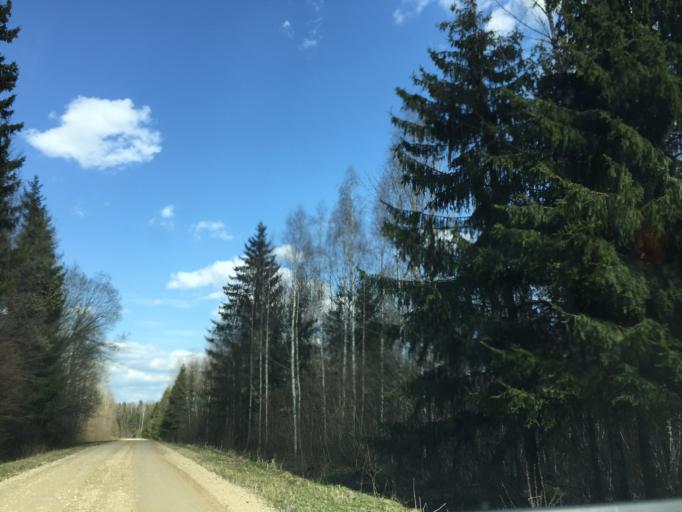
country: LV
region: Skriveri
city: Skriveri
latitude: 56.8008
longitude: 25.1744
